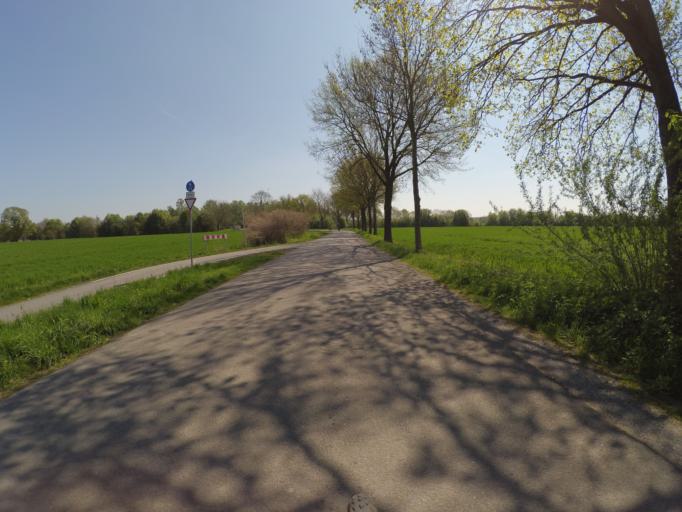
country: DE
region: North Rhine-Westphalia
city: Ludinghausen
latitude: 51.7441
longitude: 7.4618
